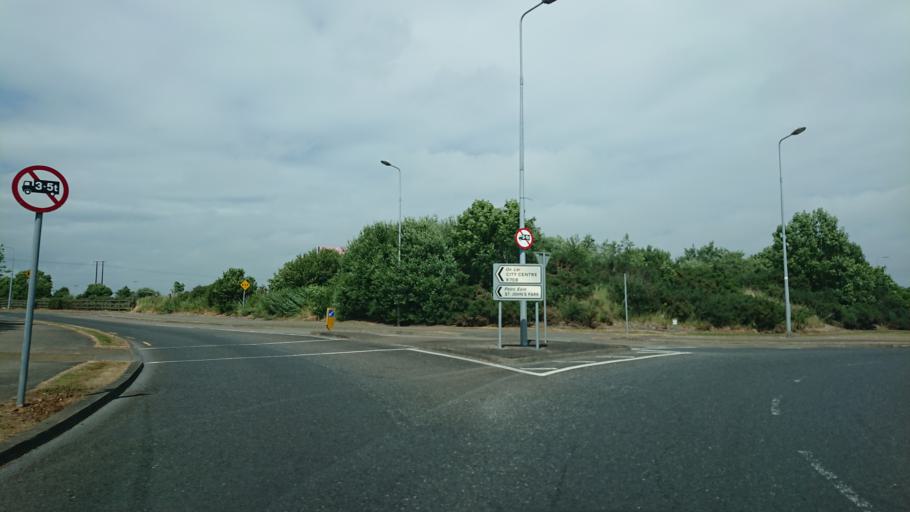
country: IE
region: Munster
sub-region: Waterford
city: Waterford
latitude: 52.2339
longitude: -7.1043
